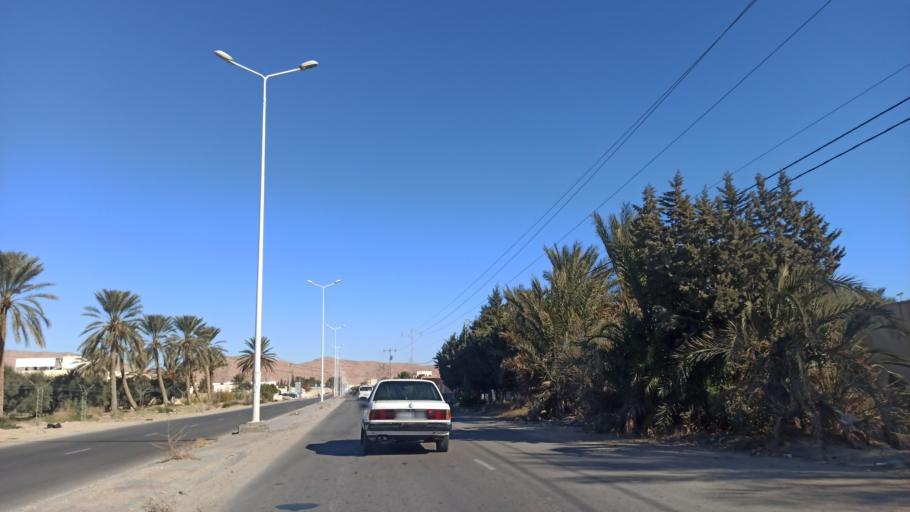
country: TN
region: Gafsa
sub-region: Gafsa Municipality
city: Gafsa
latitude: 34.4083
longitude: 8.7351
